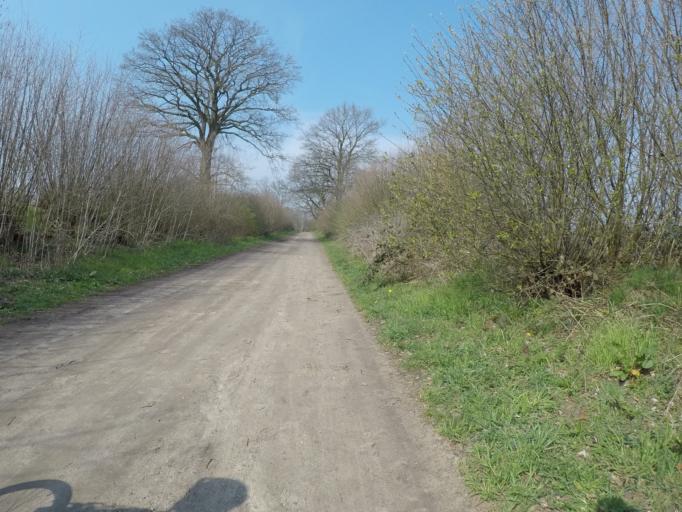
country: DE
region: Schleswig-Holstein
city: Tangstedt
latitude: 53.7239
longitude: 10.0968
